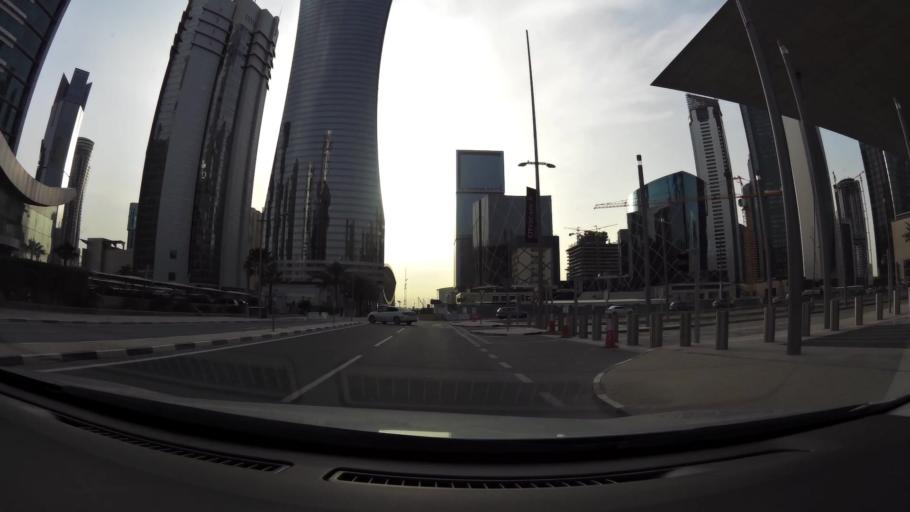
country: QA
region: Baladiyat ad Dawhah
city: Doha
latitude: 25.3221
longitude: 51.5294
